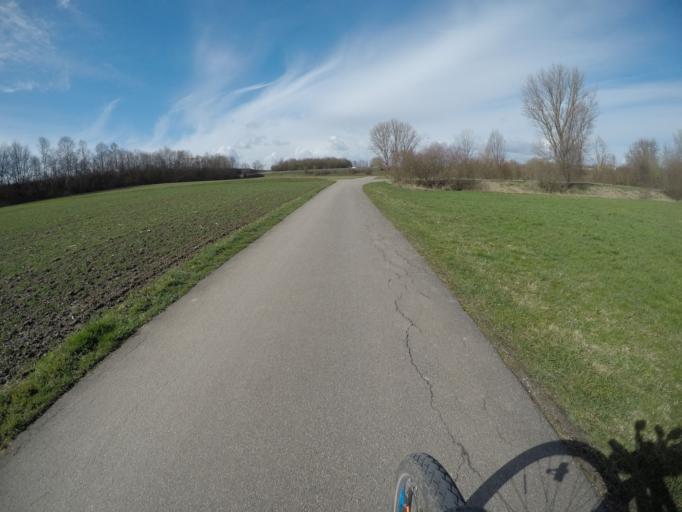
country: DE
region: Baden-Wuerttemberg
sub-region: Regierungsbezirk Stuttgart
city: Boeblingen
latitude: 48.6893
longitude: 8.9724
